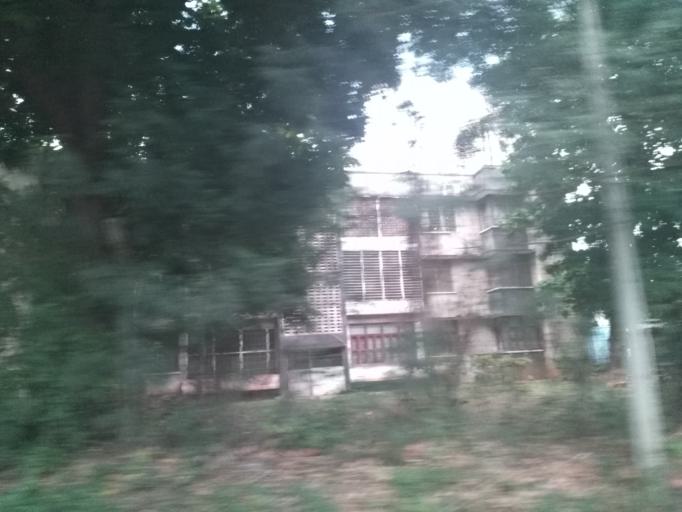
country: TZ
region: Dar es Salaam
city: Dar es Salaam
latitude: -6.7993
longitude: 39.2863
